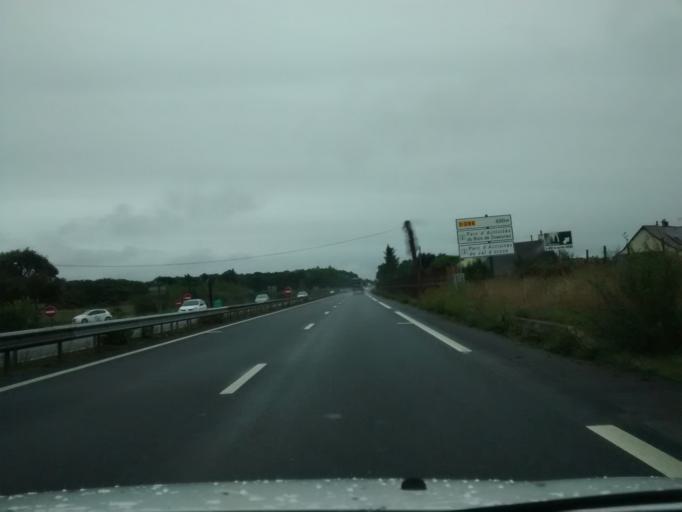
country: FR
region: Brittany
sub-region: Departement d'Ille-et-Vilaine
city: Chantepie
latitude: 48.0702
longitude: -1.6237
